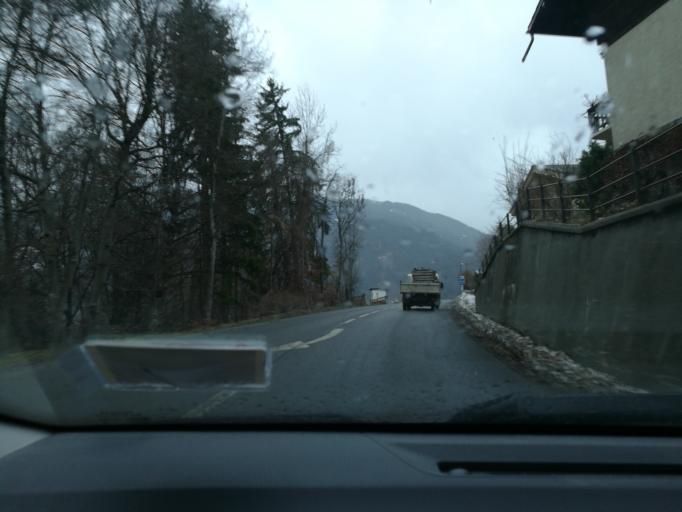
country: FR
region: Rhone-Alpes
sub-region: Departement de la Haute-Savoie
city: Saint-Gervais-les-Bains
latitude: 45.8941
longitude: 6.6983
